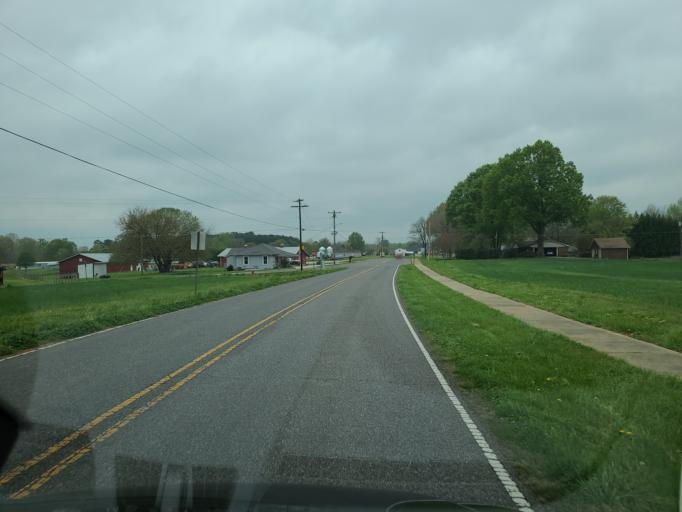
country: US
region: North Carolina
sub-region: Gaston County
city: Cherryville
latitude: 35.4246
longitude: -81.4926
